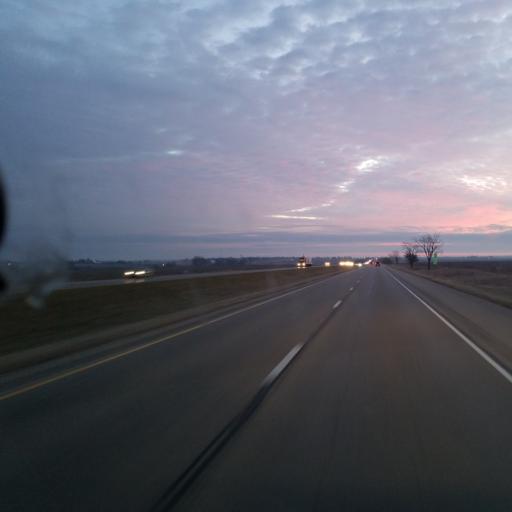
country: US
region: Illinois
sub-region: Tazewell County
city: Morton
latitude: 40.6222
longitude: -89.3733
